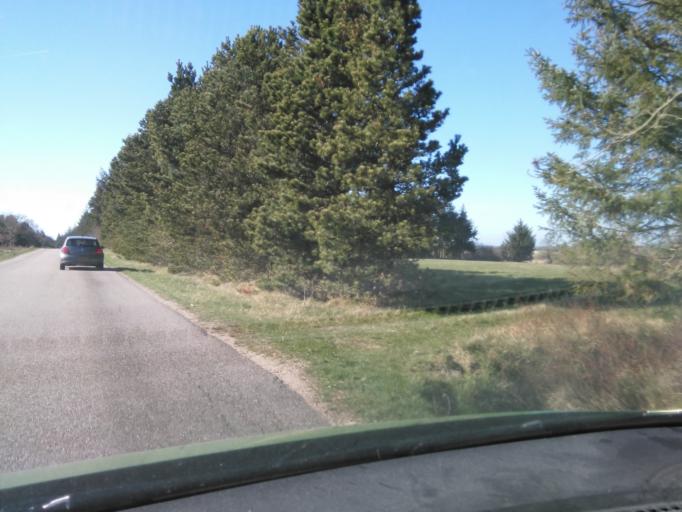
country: DK
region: South Denmark
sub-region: Varde Kommune
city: Oksbol
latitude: 55.6630
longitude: 8.2566
